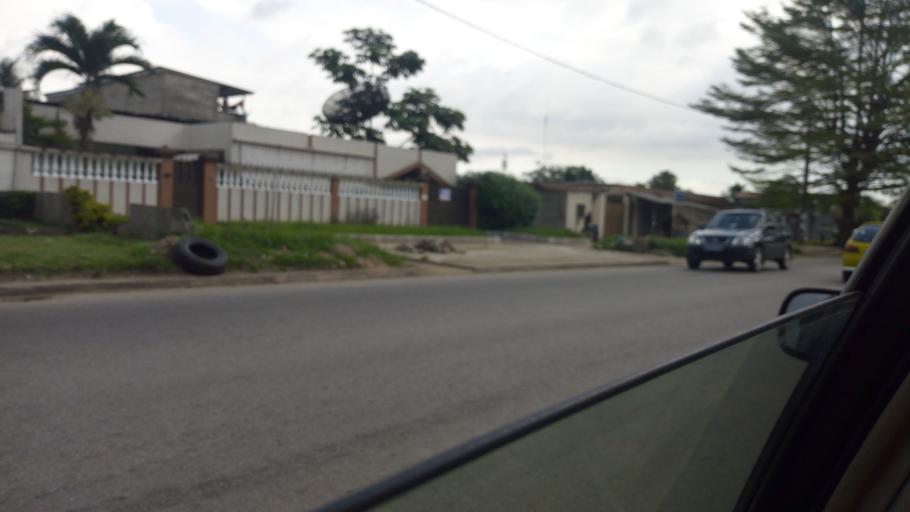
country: CI
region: Lagunes
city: Abobo
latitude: 5.4030
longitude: -3.9854
